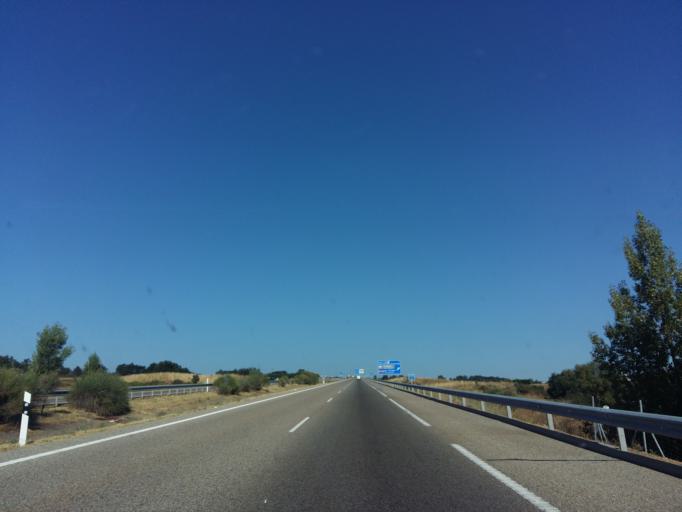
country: ES
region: Castille and Leon
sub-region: Provincia de Leon
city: San Andres del Rabanedo
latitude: 42.5721
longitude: -5.6083
